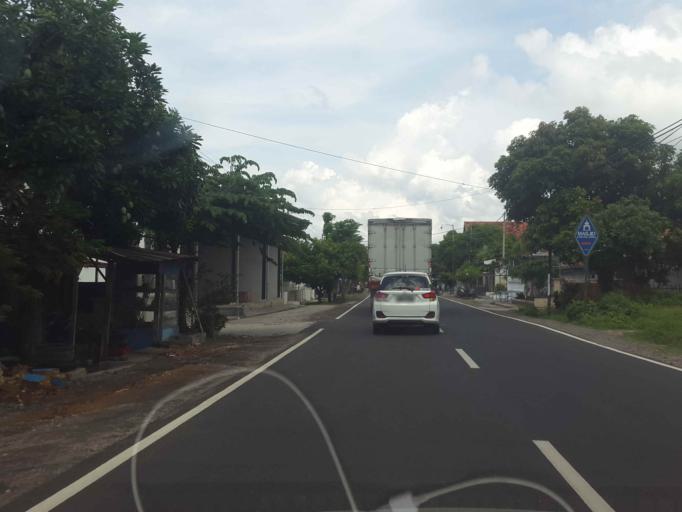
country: ID
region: East Java
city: Biyan
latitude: -7.1137
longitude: 113.7244
